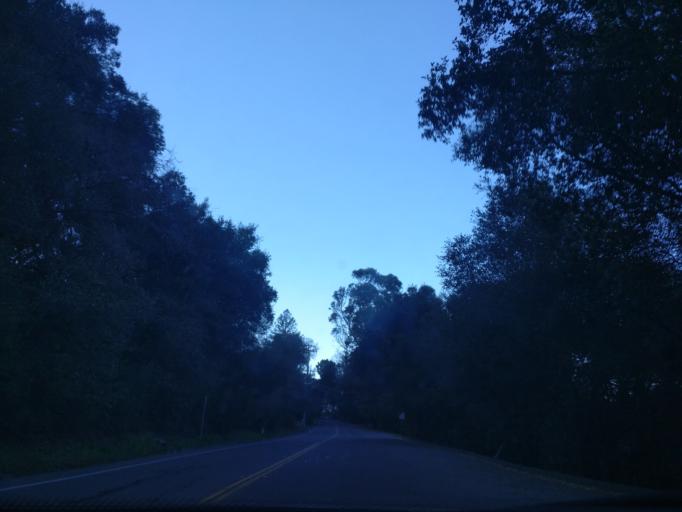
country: US
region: California
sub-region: Contra Costa County
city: Orinda
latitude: 37.8861
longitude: -122.1939
